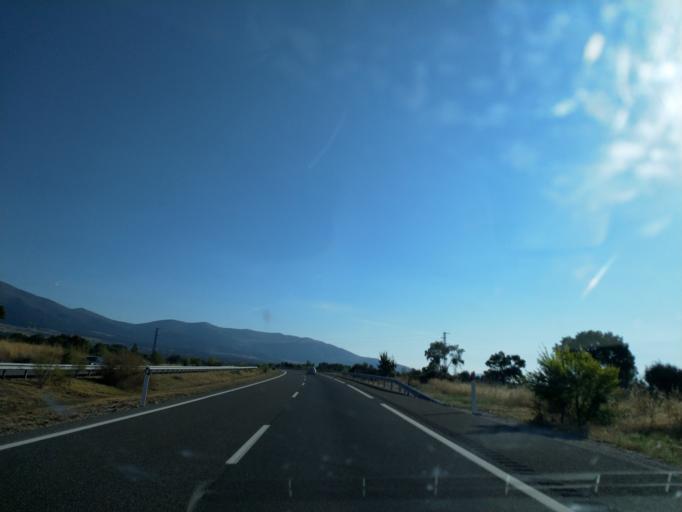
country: ES
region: Castille and Leon
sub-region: Provincia de Segovia
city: Segovia
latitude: 40.8910
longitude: -4.1147
